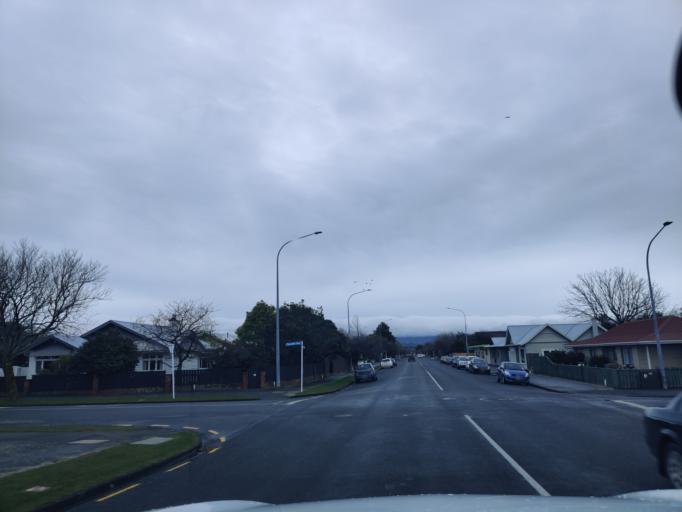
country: NZ
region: Manawatu-Wanganui
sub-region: Palmerston North City
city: Palmerston North
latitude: -40.3414
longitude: 175.6138
